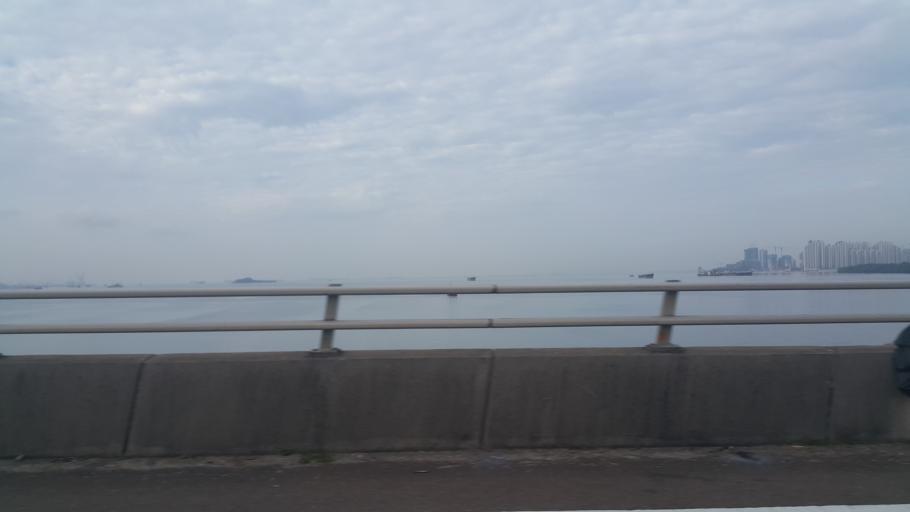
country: MY
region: Johor
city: Johor Bahru
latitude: 1.3555
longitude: 103.6266
